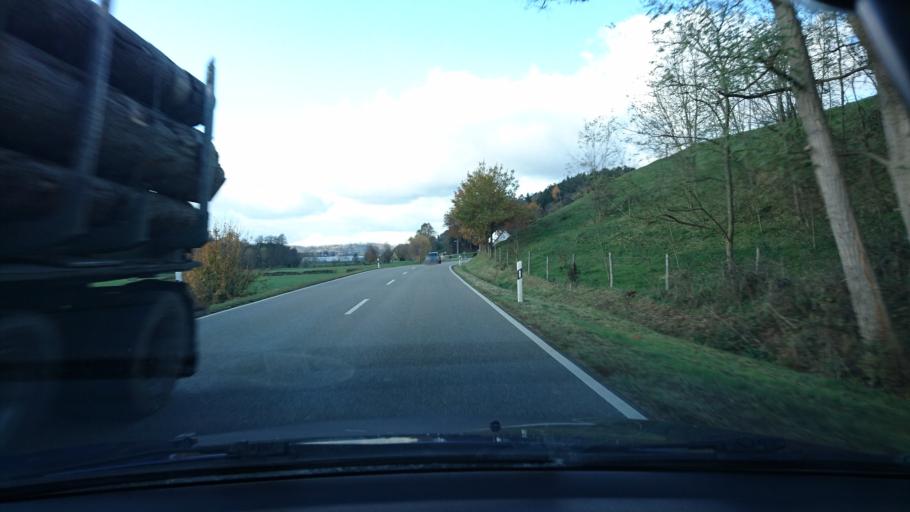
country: DE
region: Baden-Wuerttemberg
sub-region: Regierungsbezirk Stuttgart
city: Neuler
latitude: 48.8954
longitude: 10.0446
